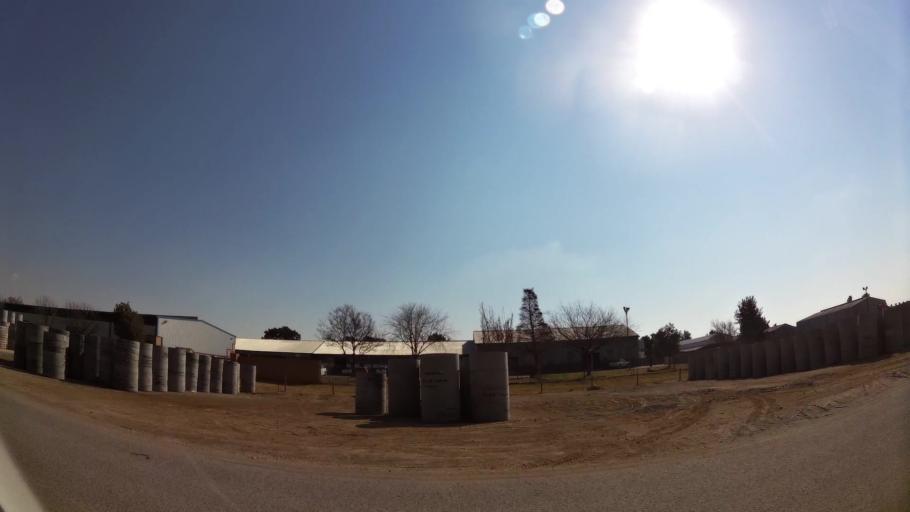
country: ZA
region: Gauteng
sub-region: Ekurhuleni Metropolitan Municipality
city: Benoni
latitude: -26.2020
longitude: 28.3139
